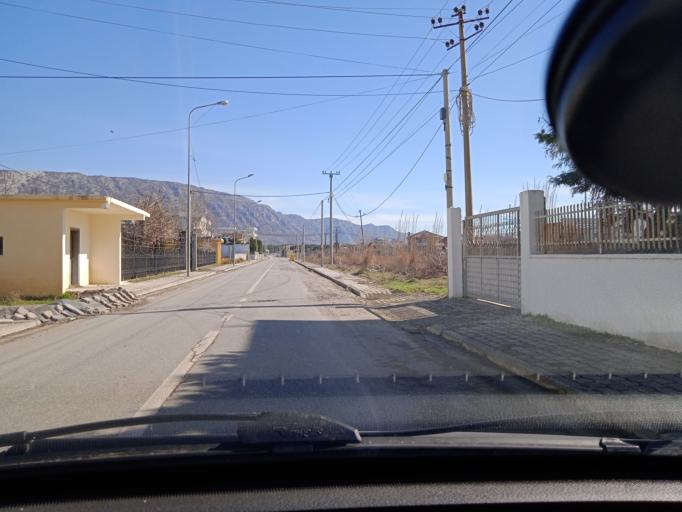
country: AL
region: Shkoder
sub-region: Rrethi i Shkodres
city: Velipoje
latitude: 41.8656
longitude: 19.4339
